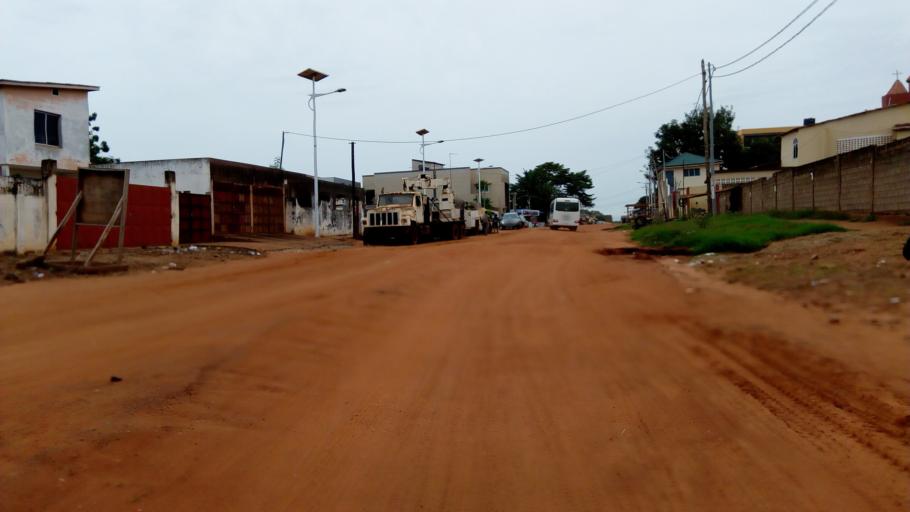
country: TG
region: Maritime
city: Lome
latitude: 6.1607
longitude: 1.2204
